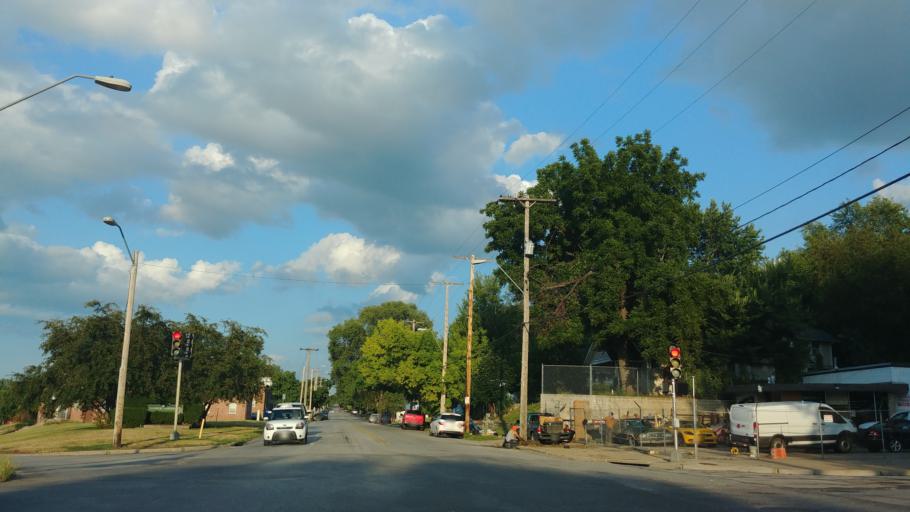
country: US
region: Missouri
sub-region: Clay County
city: North Kansas City
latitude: 39.0978
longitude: -94.5236
